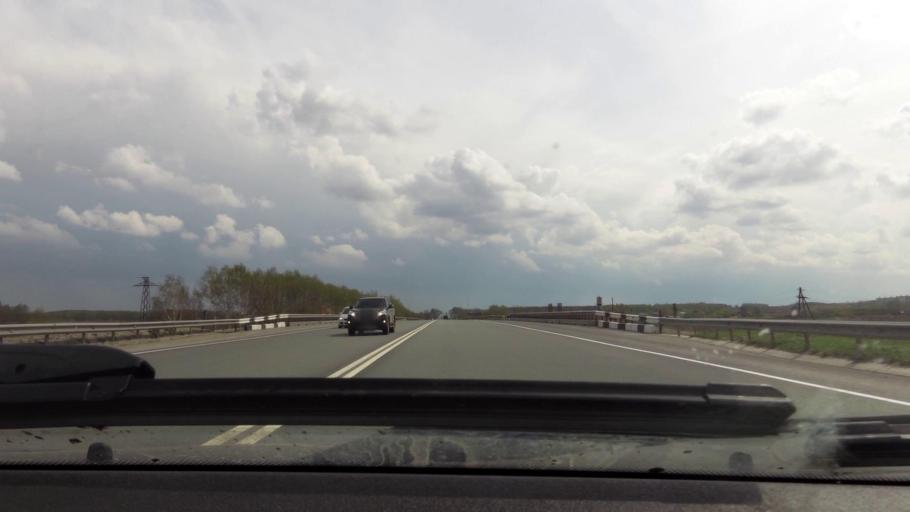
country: RU
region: Rjazan
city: Bagramovo
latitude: 54.7364
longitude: 39.4520
